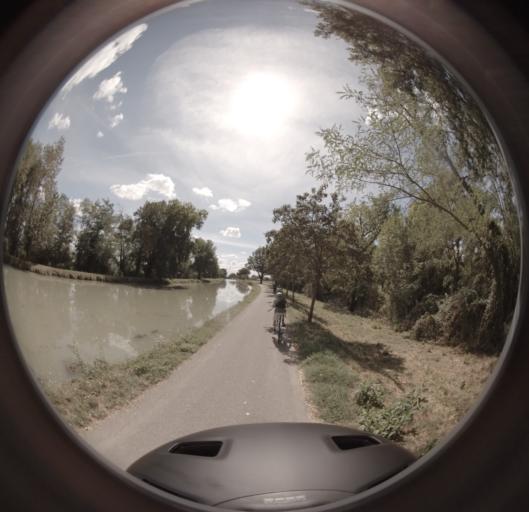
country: FR
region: Midi-Pyrenees
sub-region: Departement du Tarn-et-Garonne
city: Moissac
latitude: 44.0757
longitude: 1.0984
